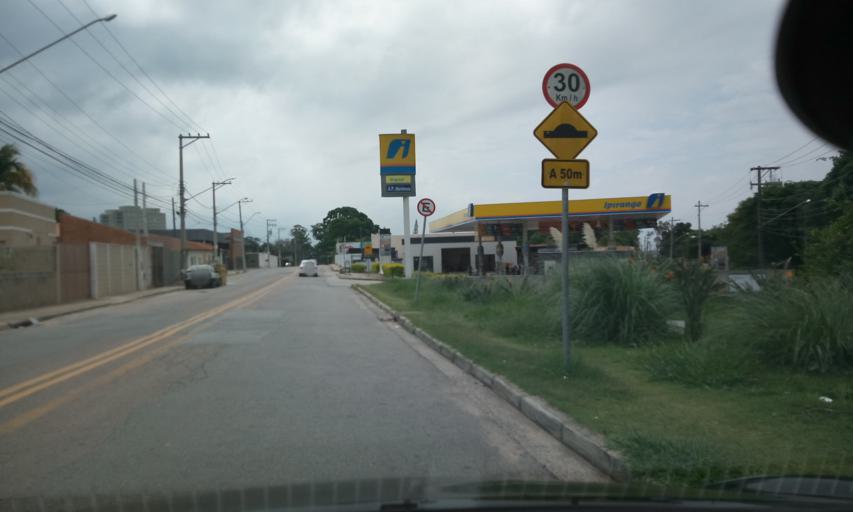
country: BR
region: Sao Paulo
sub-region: Itupeva
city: Itupeva
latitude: -23.1871
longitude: -46.9849
